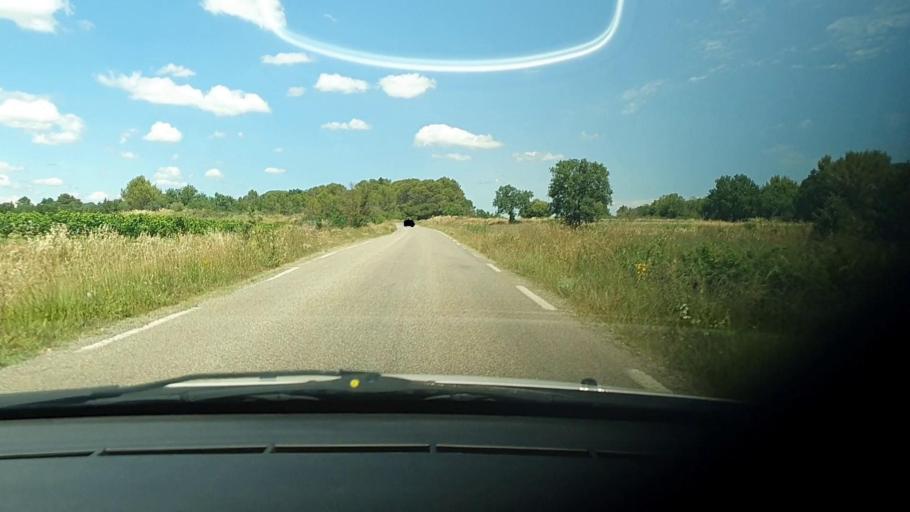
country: FR
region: Languedoc-Roussillon
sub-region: Departement du Gard
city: Blauzac
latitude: 43.9720
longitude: 4.3684
